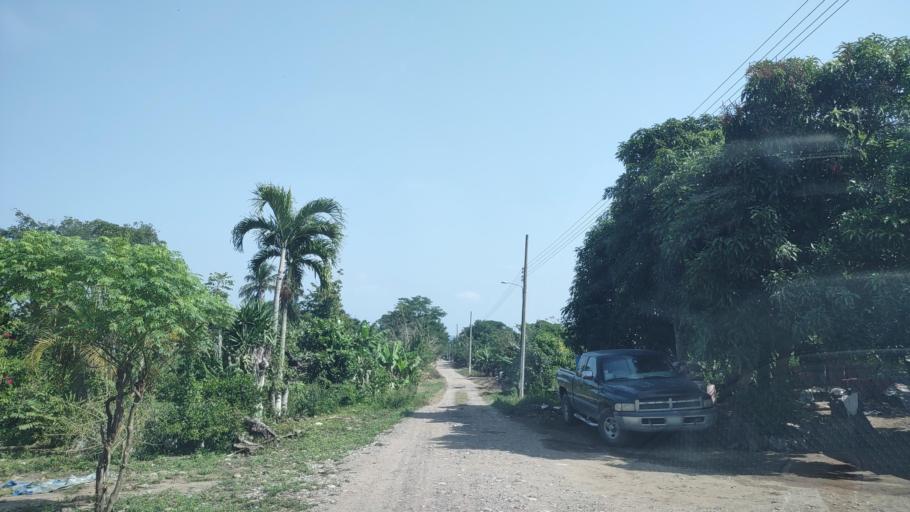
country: MX
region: Puebla
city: Espinal
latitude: 20.2607
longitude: -97.3129
